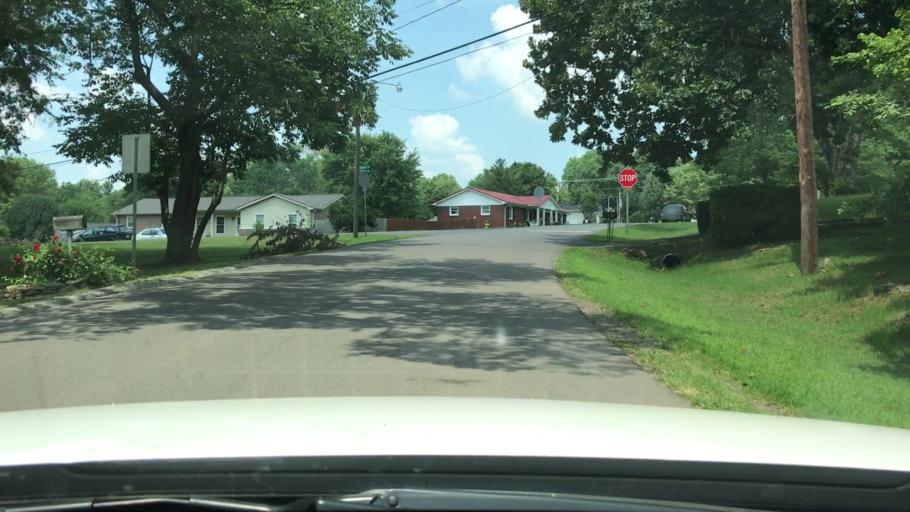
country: US
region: Tennessee
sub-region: Sumner County
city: Gallatin
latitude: 36.3664
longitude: -86.4696
